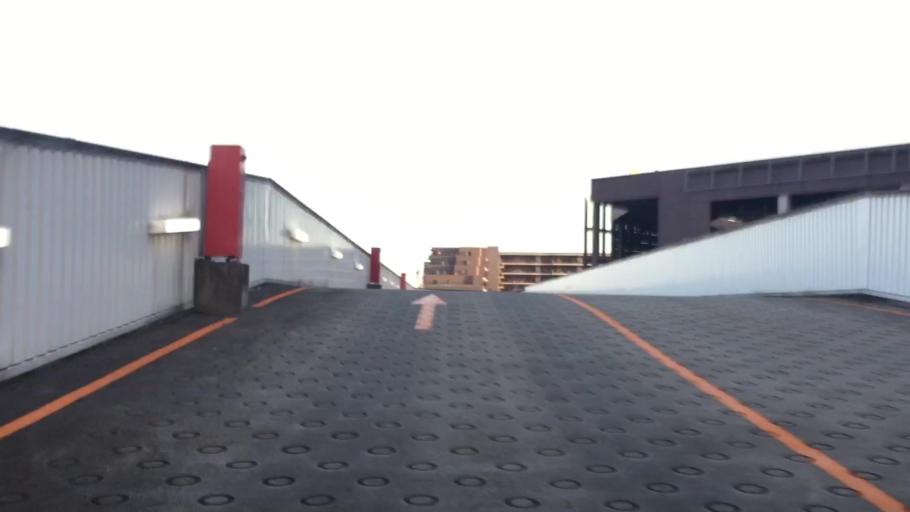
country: JP
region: Saitama
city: Yoshikawa
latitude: 35.8783
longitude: 139.8265
